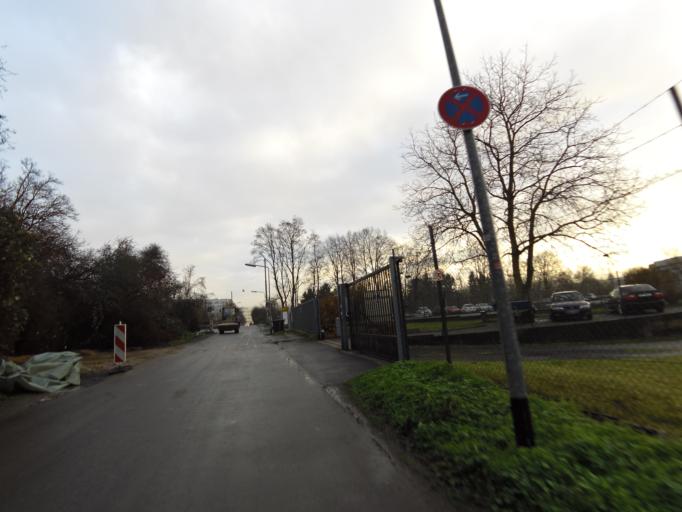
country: DE
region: Hesse
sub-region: Regierungsbezirk Darmstadt
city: Eschborn
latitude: 50.1259
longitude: 8.5765
